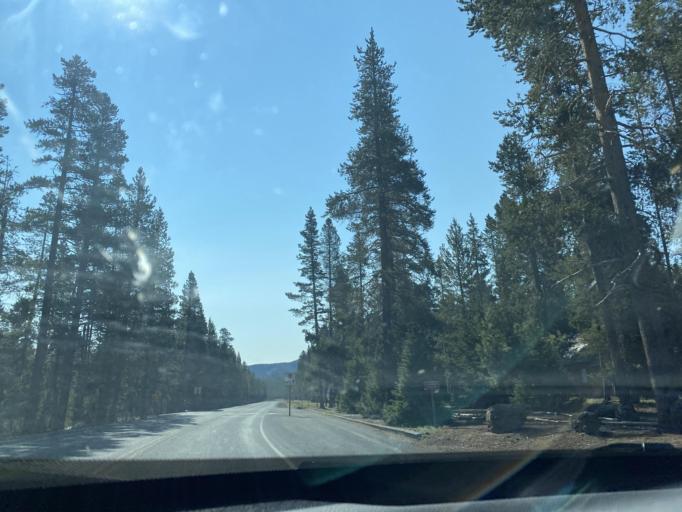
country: US
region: Oregon
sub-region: Deschutes County
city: Three Rivers
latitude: 43.7122
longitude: -121.2774
